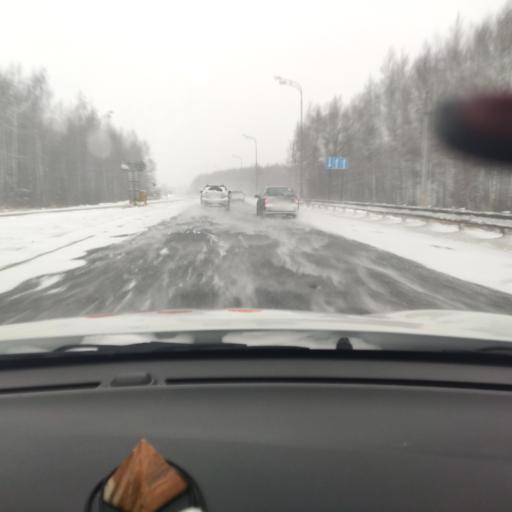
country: RU
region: Tatarstan
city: Verkhniy Uslon
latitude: 55.7100
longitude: 48.8885
